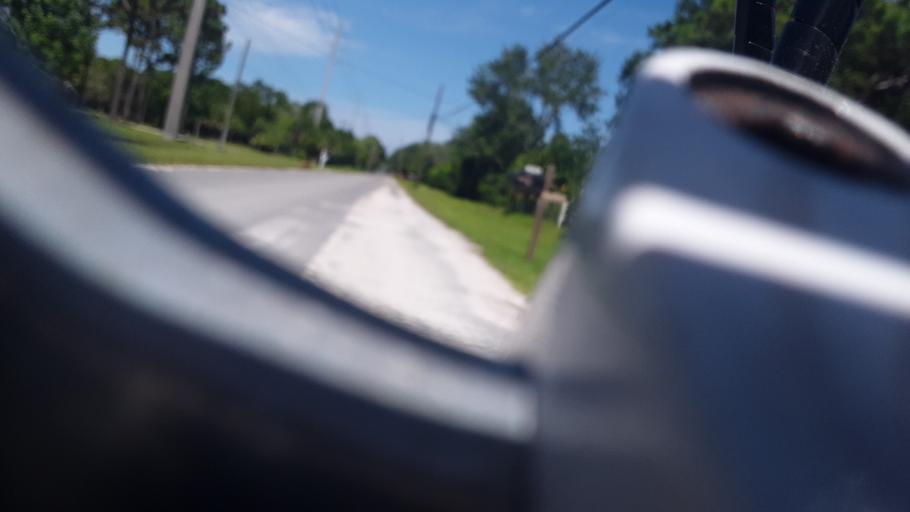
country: US
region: Florida
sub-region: Brevard County
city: Malabar
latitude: 27.9911
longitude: -80.6119
